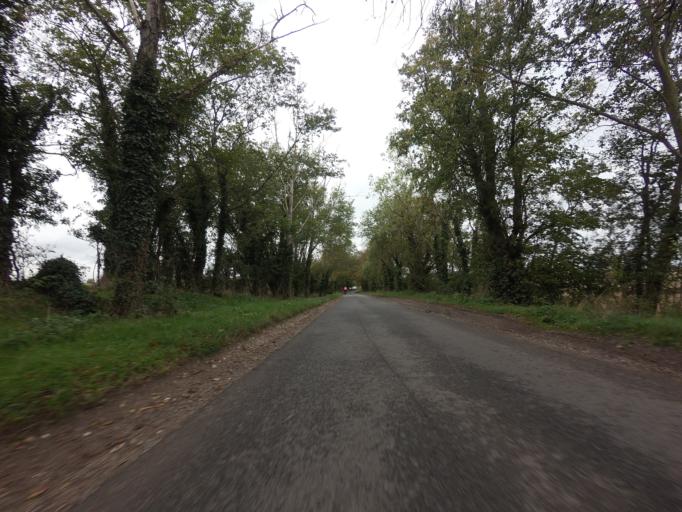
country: GB
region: England
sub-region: Cambridgeshire
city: Duxford
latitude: 52.0451
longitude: 0.1631
